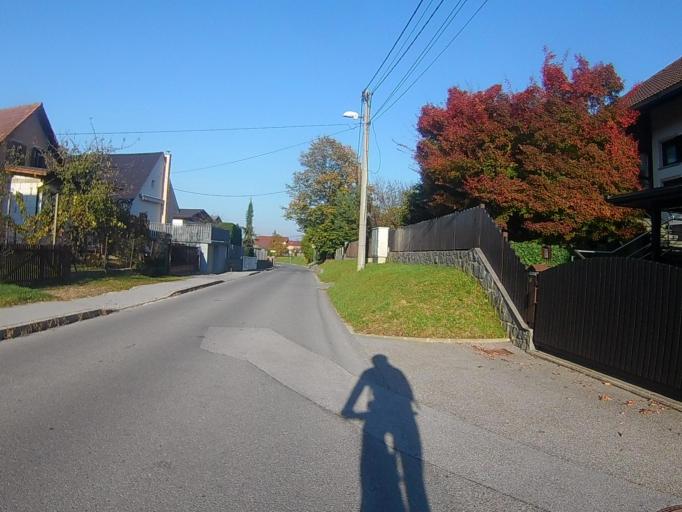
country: SI
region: Hoce-Slivnica
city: Spodnje Hoce
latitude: 46.4962
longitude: 15.6375
